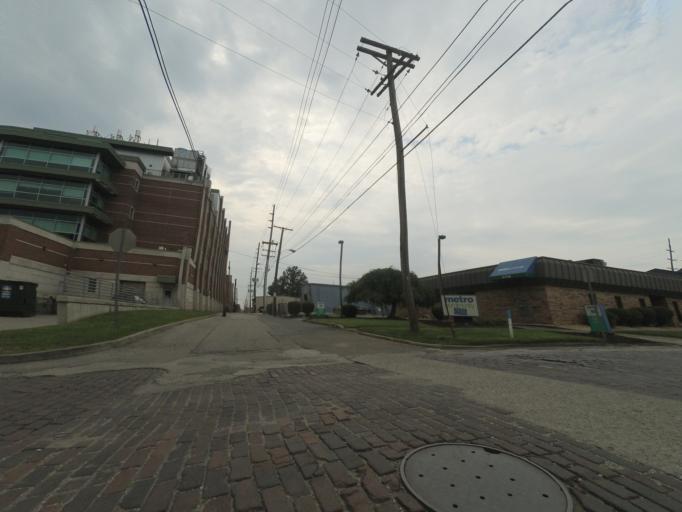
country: US
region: West Virginia
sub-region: Cabell County
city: Huntington
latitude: 38.4255
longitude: -82.4268
